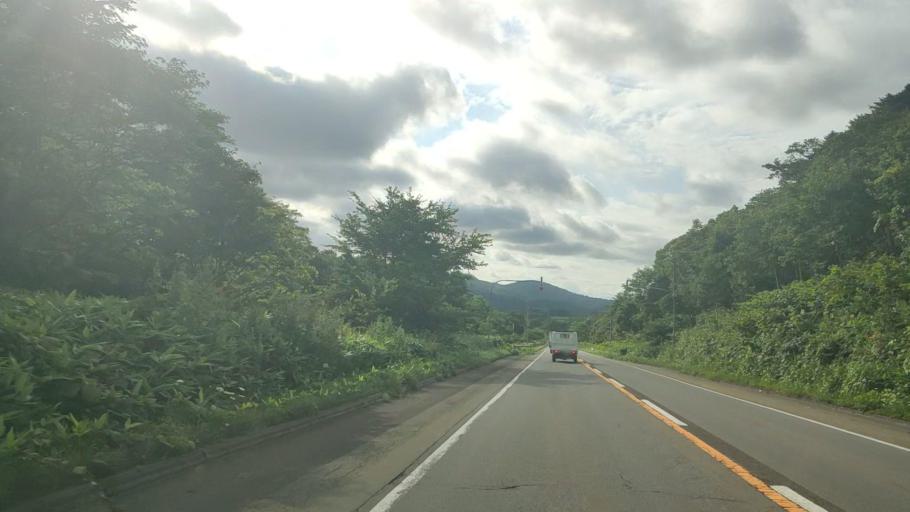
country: JP
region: Hokkaido
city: Niseko Town
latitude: 42.5988
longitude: 140.4990
